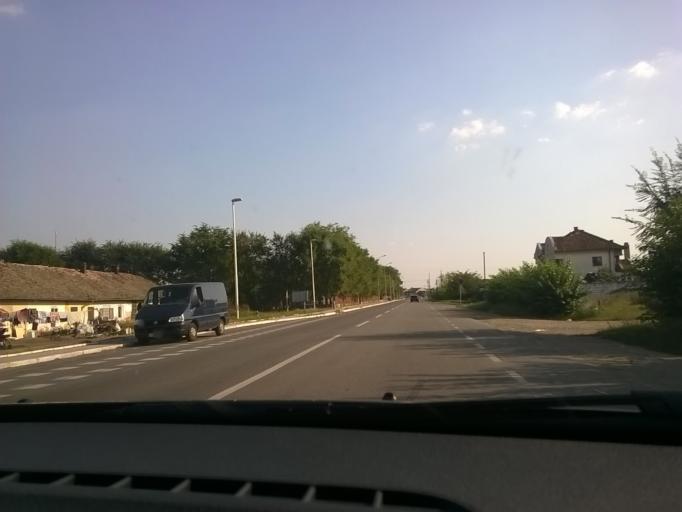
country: RS
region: Autonomna Pokrajina Vojvodina
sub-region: Juznobanatski Okrug
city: Vrsac
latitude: 45.1317
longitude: 21.2873
